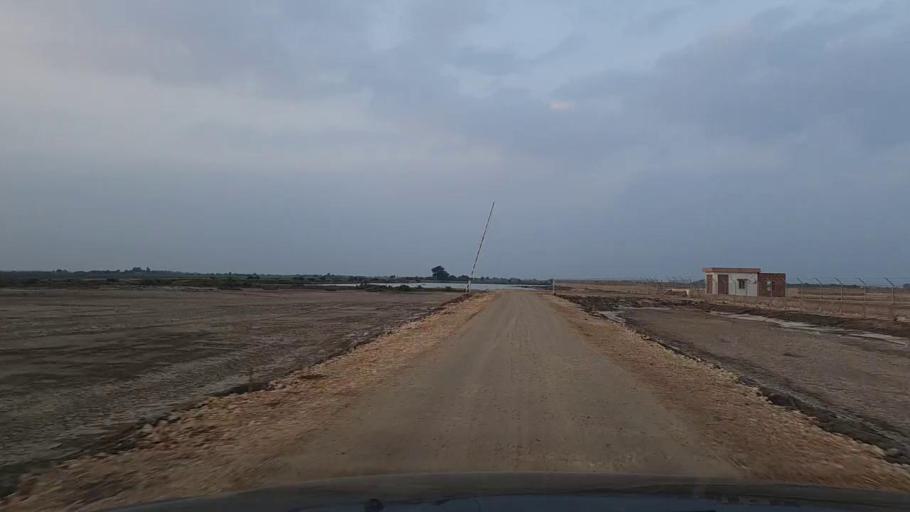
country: PK
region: Sindh
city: Jati
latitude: 24.4934
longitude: 68.3918
